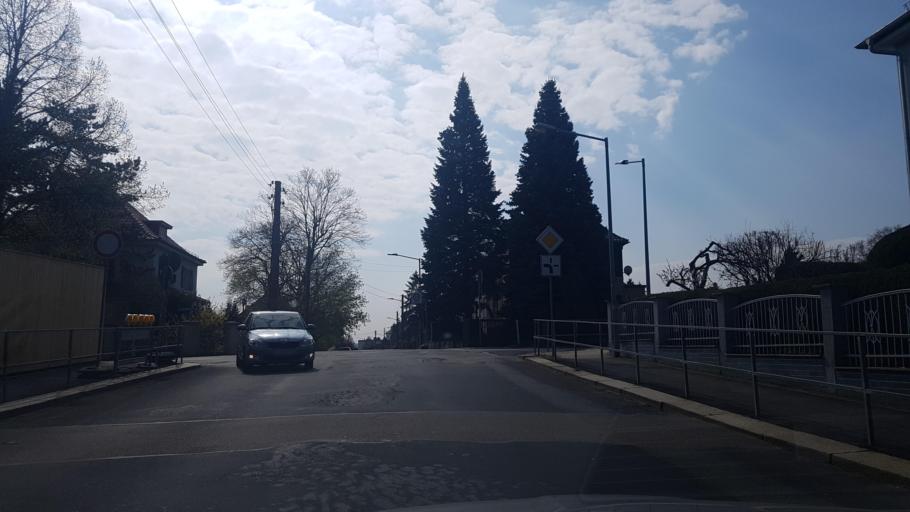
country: DE
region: Saxony
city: Meerane
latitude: 50.8431
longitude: 12.4571
